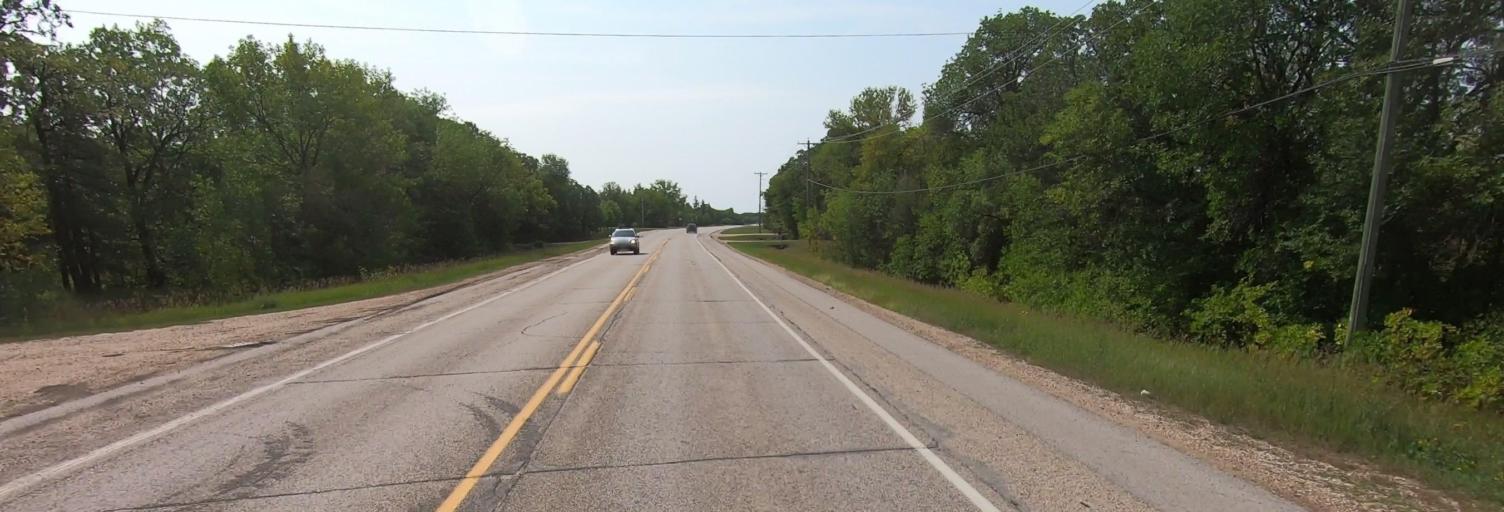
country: CA
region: Manitoba
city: Niverville
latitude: 49.7183
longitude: -97.0903
